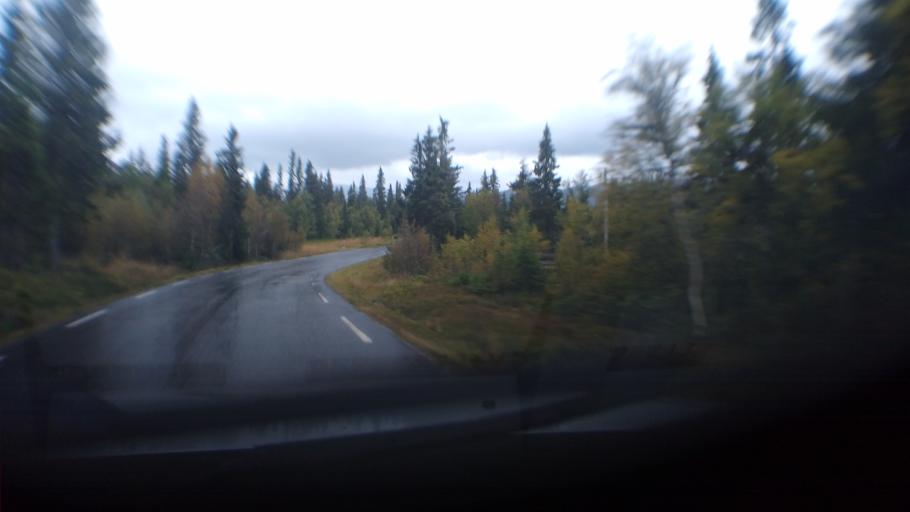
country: NO
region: Oppland
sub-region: Ringebu
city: Ringebu
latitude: 61.6093
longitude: 10.0716
